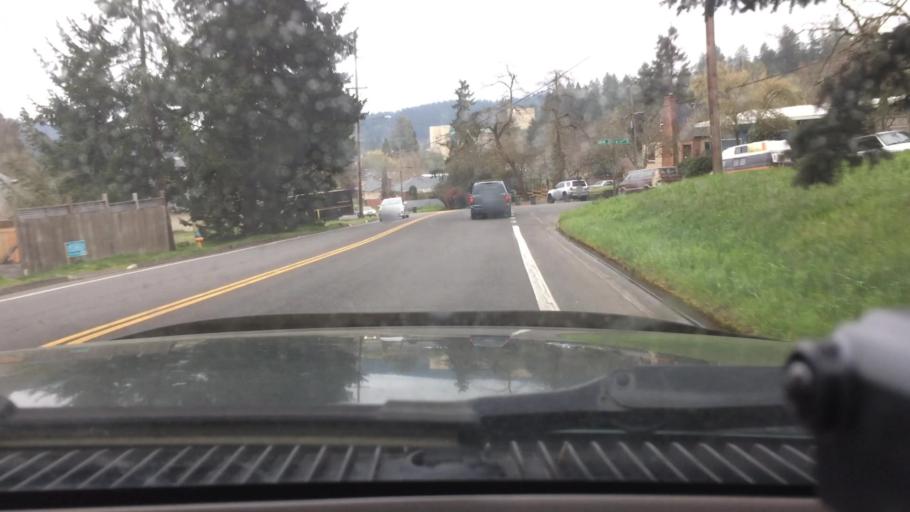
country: US
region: Oregon
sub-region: Lane County
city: Eugene
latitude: 44.0264
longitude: -123.0994
